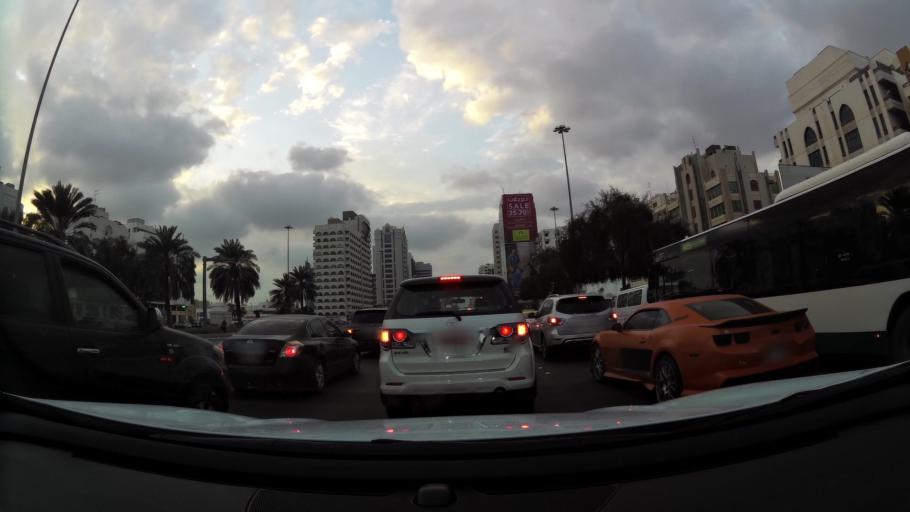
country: AE
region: Abu Dhabi
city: Abu Dhabi
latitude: 24.4570
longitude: 54.3834
